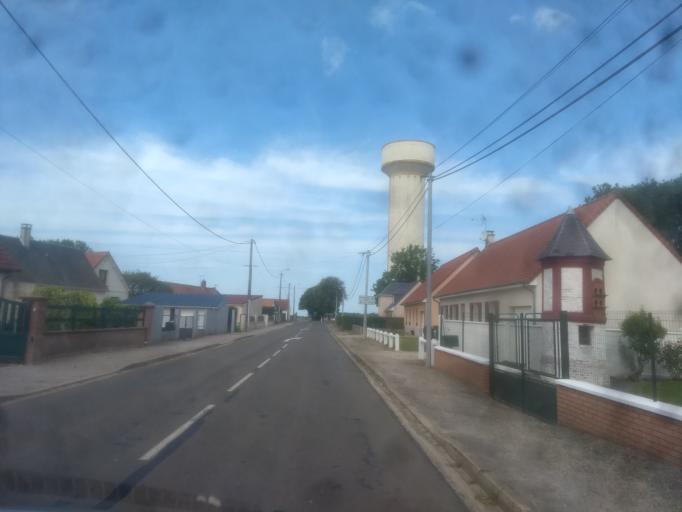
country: FR
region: Picardie
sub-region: Departement de la Somme
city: Nouvion
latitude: 50.1890
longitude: 1.8255
